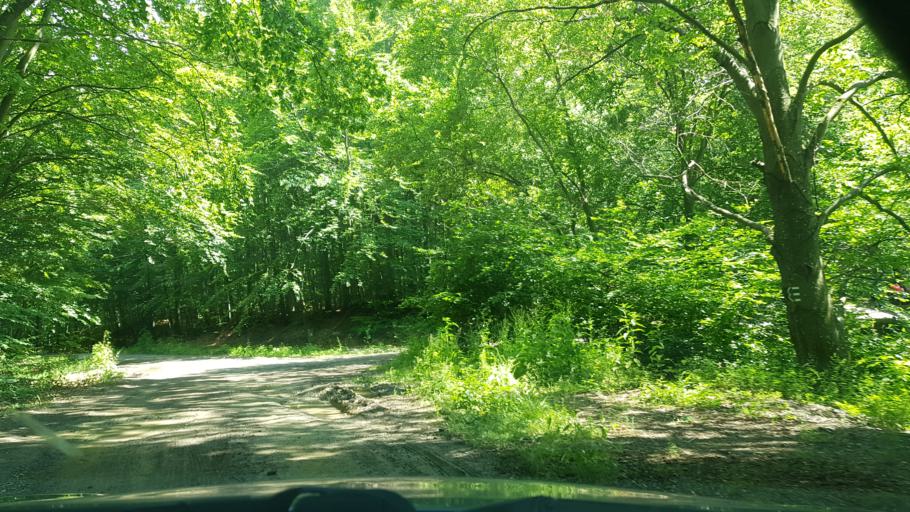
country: SK
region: Kosicky
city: Secovce
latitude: 48.5704
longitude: 21.4946
